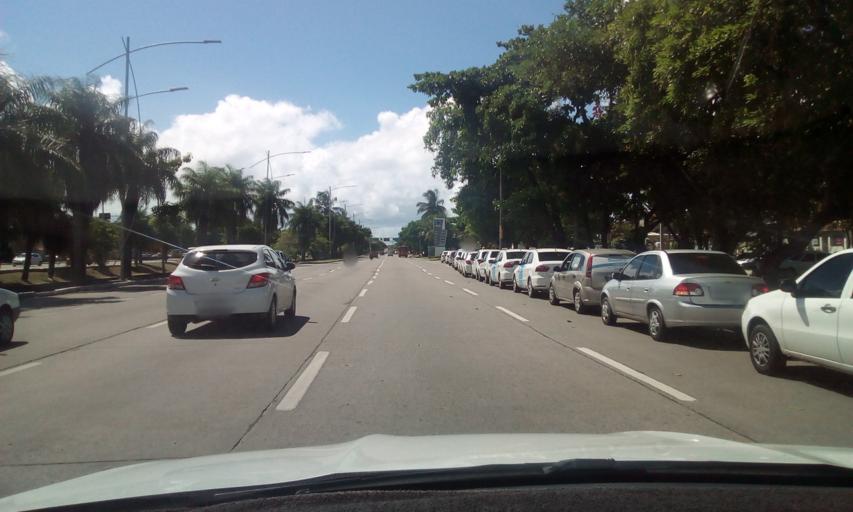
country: BR
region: Pernambuco
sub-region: Recife
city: Recife
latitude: -8.0412
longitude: -34.8815
